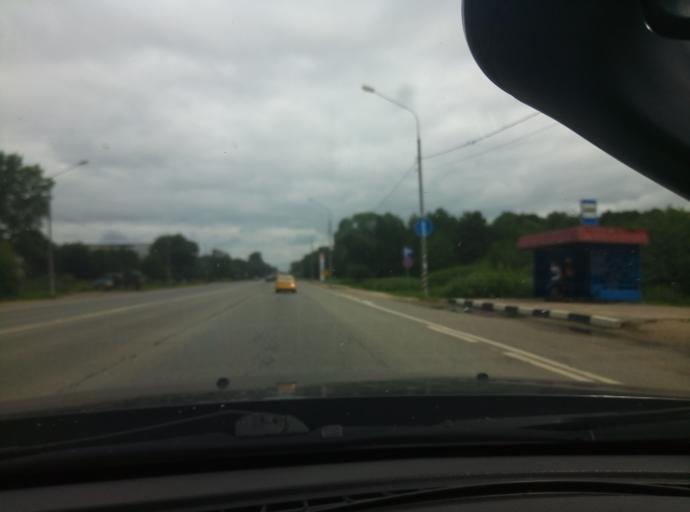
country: RU
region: Kaluga
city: Obninsk
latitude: 55.0938
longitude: 36.6362
